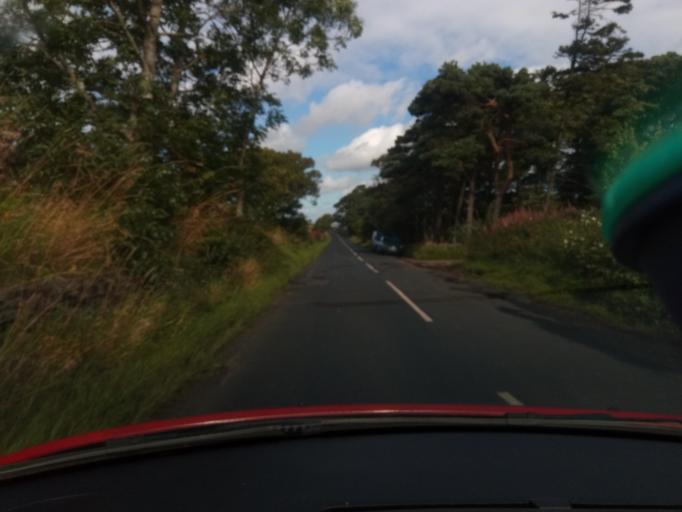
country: GB
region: Scotland
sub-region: The Scottish Borders
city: Melrose
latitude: 55.5755
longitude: -2.7327
